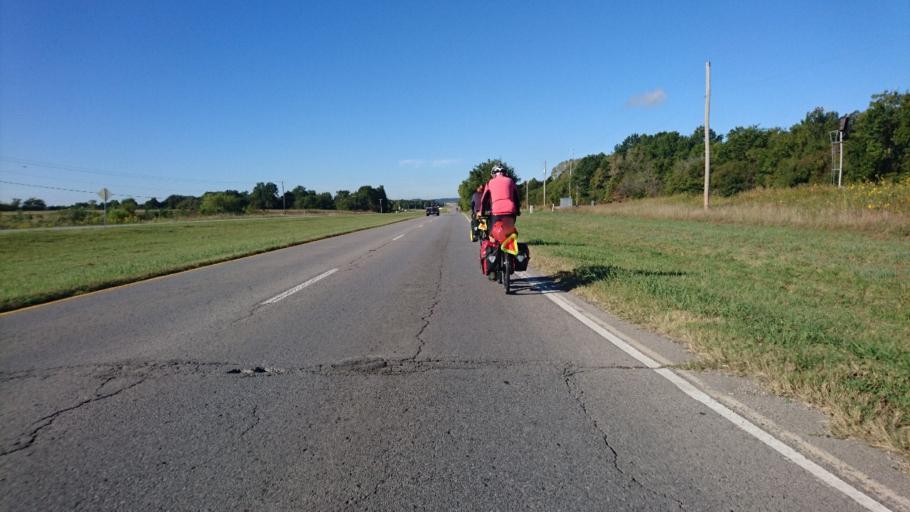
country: US
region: Oklahoma
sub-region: Rogers County
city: Verdigris
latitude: 36.2335
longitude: -95.6915
